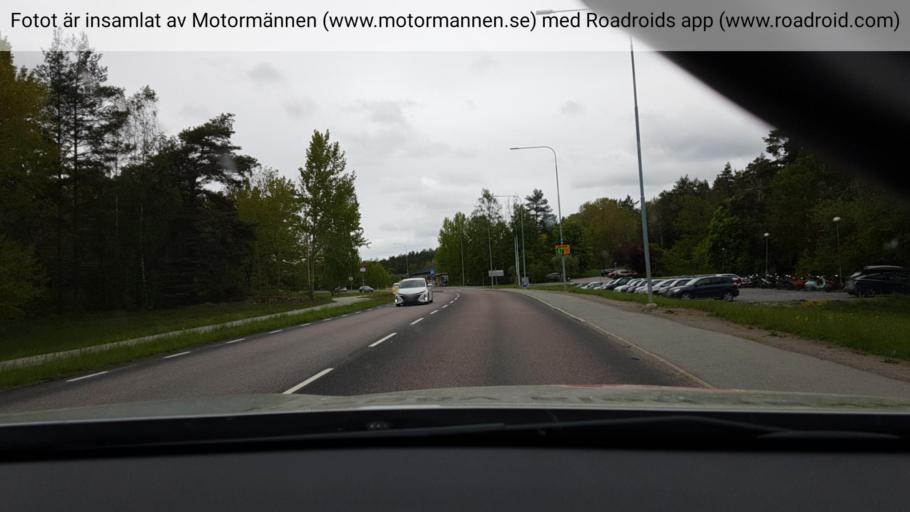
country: SE
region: Stockholm
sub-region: Lidingo
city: Brevik
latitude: 59.3552
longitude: 18.1661
